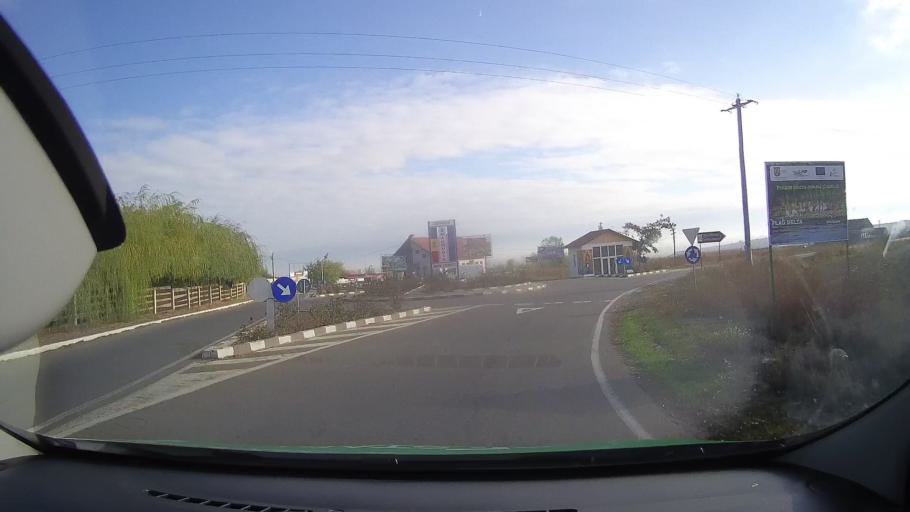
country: RO
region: Tulcea
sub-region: Comuna Mahmudia
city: Mahmudia
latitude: 45.0788
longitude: 29.0782
